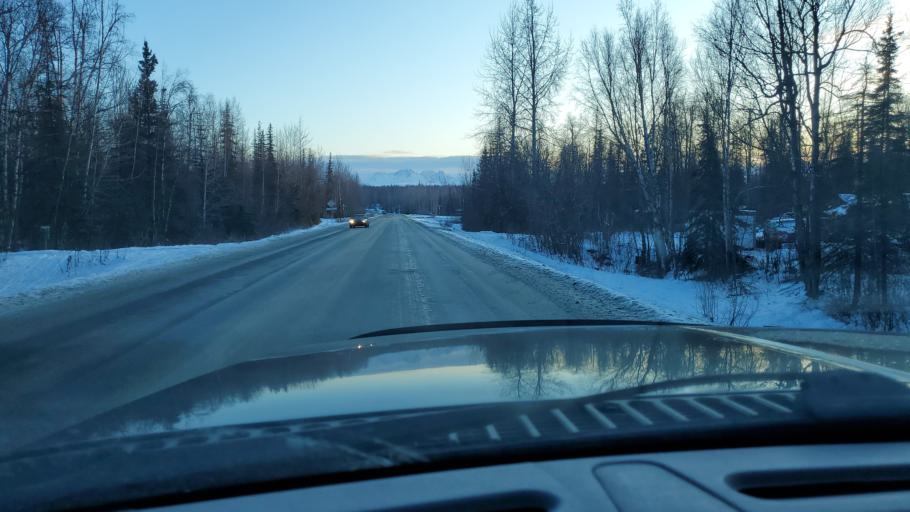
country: US
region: Alaska
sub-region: Matanuska-Susitna Borough
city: Fishhook
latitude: 61.6876
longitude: -149.2410
